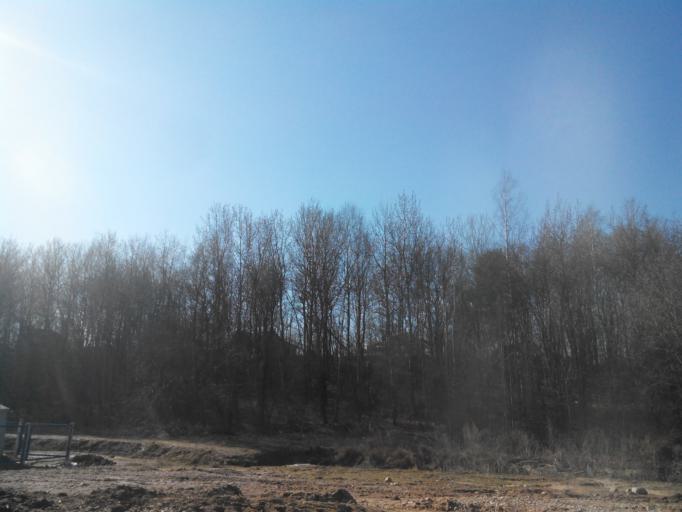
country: BY
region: Minsk
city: Zhdanovichy
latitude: 53.9220
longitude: 27.3977
